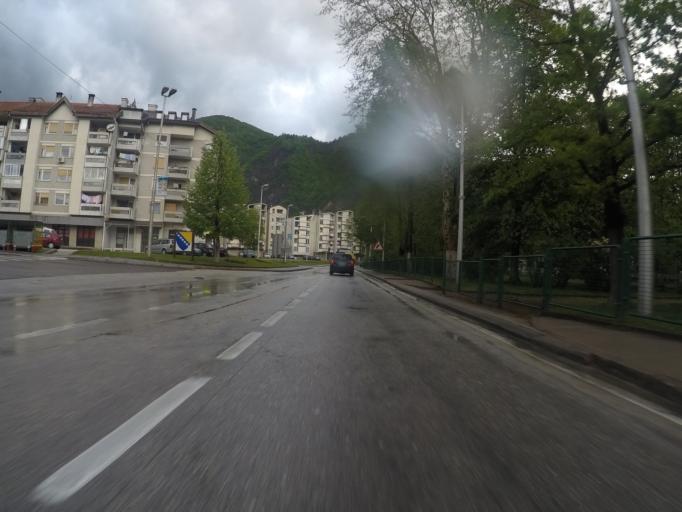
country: BA
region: Federation of Bosnia and Herzegovina
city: Jablanica
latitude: 43.6614
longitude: 17.7631
